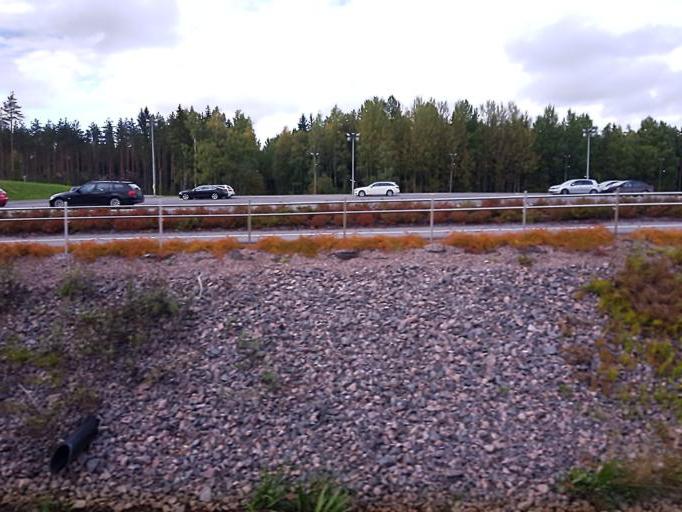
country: FI
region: Uusimaa
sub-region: Helsinki
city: Helsinki
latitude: 60.2548
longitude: 24.9188
